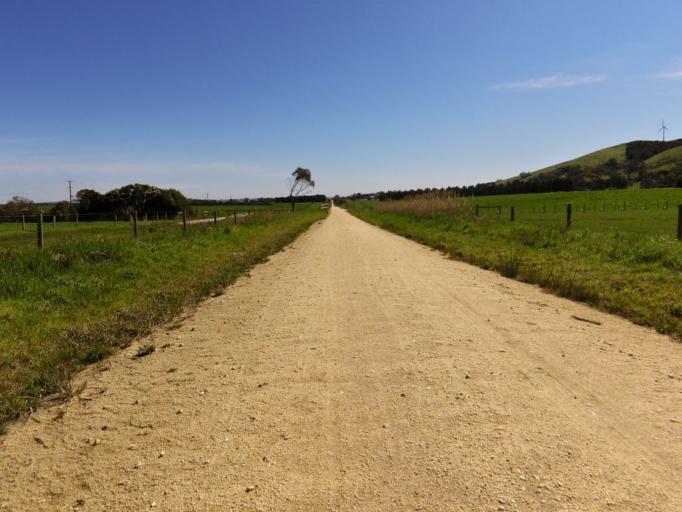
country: AU
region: Victoria
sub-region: Latrobe
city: Morwell
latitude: -38.6697
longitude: 146.3528
